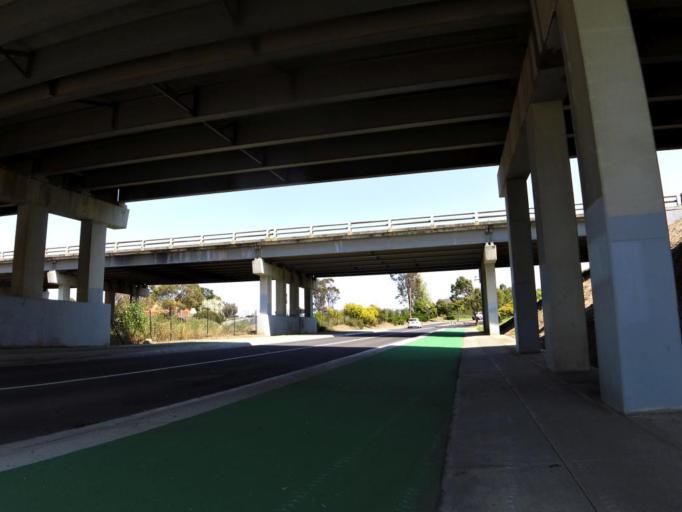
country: AU
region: Victoria
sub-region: Moreland
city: Gowanbrae
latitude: -37.7098
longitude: 144.8910
